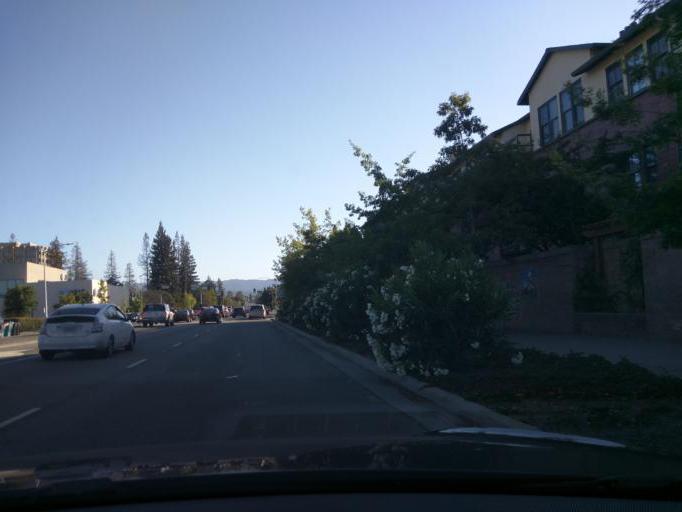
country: US
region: California
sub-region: Santa Clara County
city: Palo Alto
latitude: 37.4242
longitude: -122.1412
